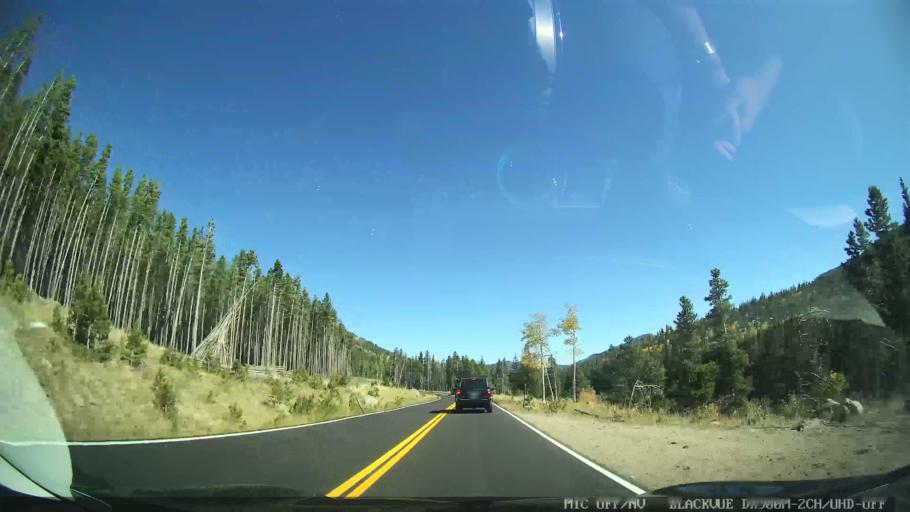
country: US
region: Colorado
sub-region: Larimer County
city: Estes Park
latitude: 40.3169
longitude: -105.6308
